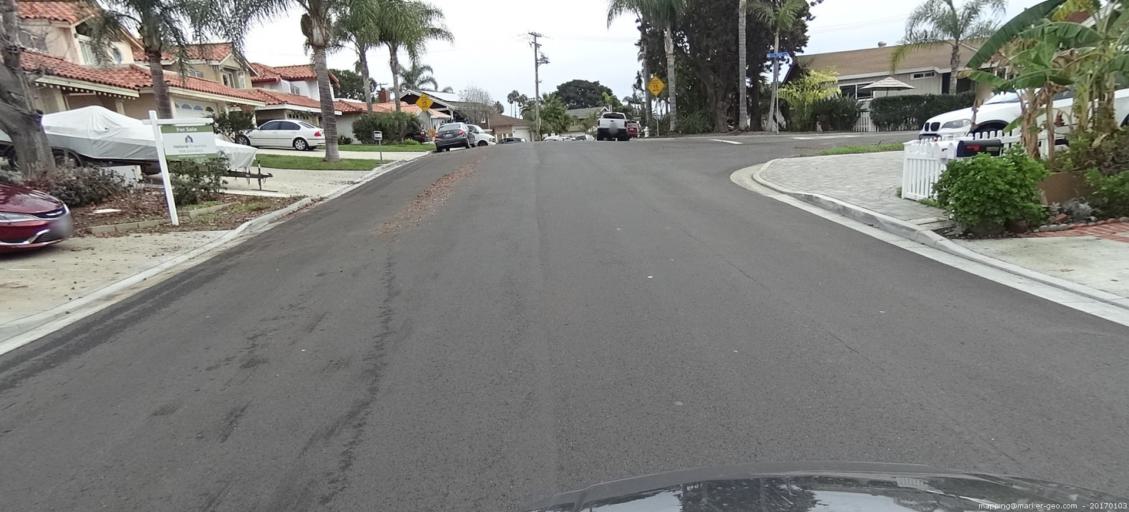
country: US
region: California
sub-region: Orange County
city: San Juan Capistrano
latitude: 33.4613
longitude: -117.6565
